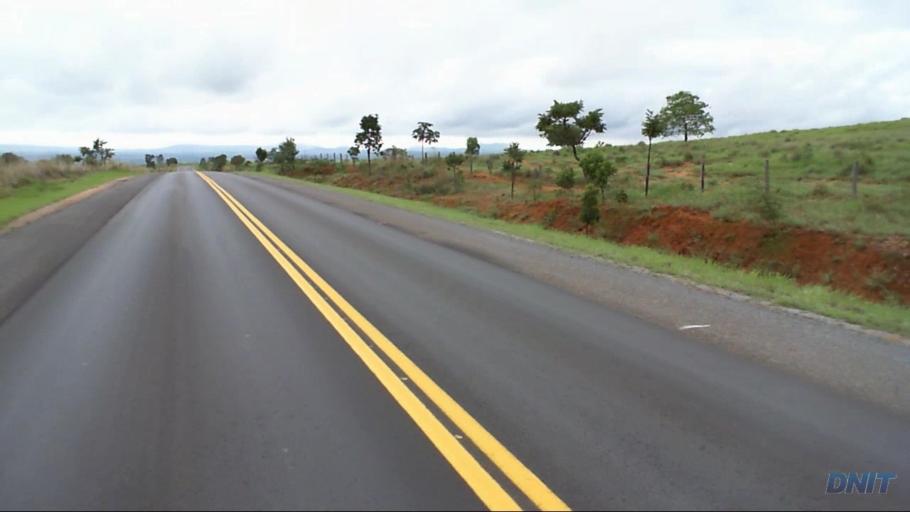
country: BR
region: Goias
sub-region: Padre Bernardo
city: Padre Bernardo
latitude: -15.2173
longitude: -48.5140
